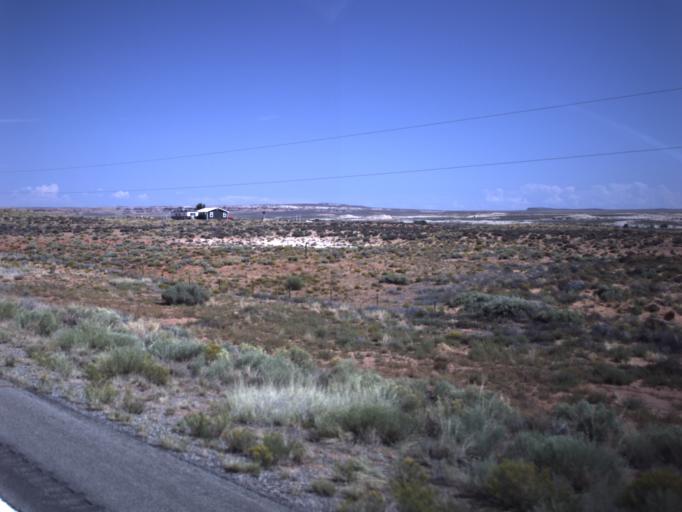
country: US
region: Utah
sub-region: San Juan County
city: Blanding
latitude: 37.0833
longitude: -109.5480
